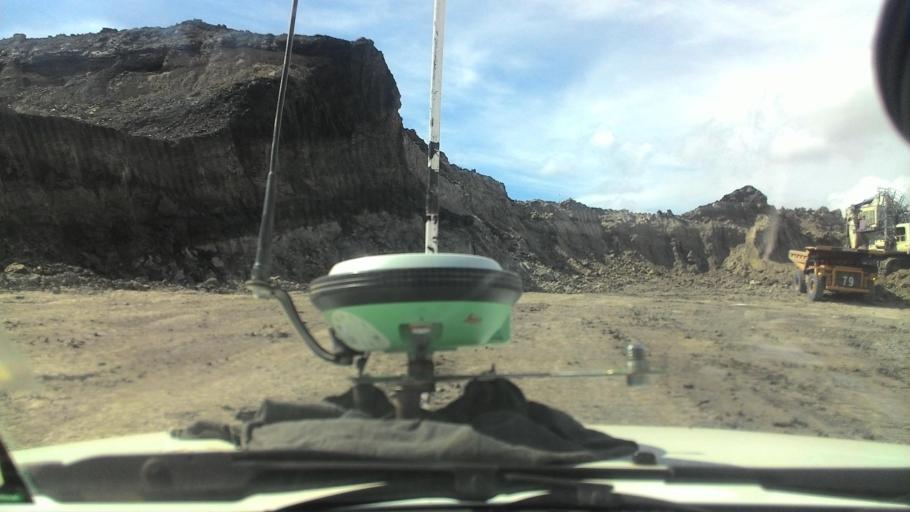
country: ID
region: South Kalimantan
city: Mungkuruyam
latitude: -2.1427
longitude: 115.5823
